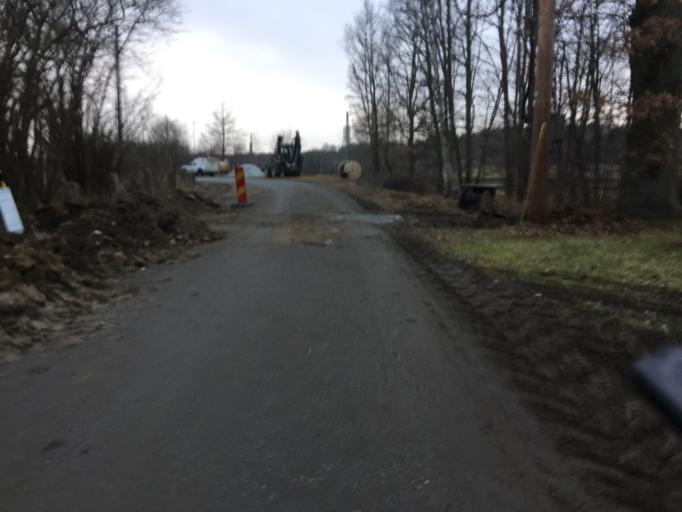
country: SE
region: Blekinge
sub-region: Karlshamns Kommun
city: Morrum
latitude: 56.1762
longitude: 14.7776
